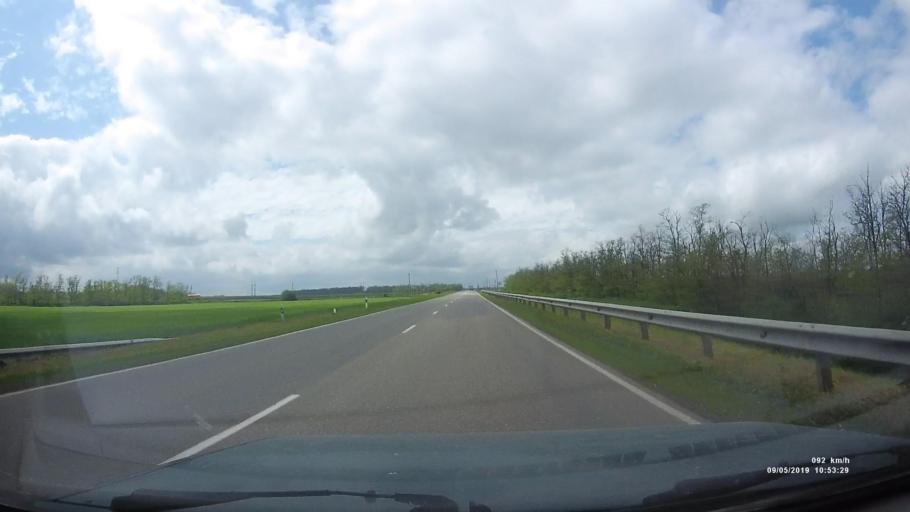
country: RU
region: Rostov
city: Peshkovo
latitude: 46.8886
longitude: 39.3419
